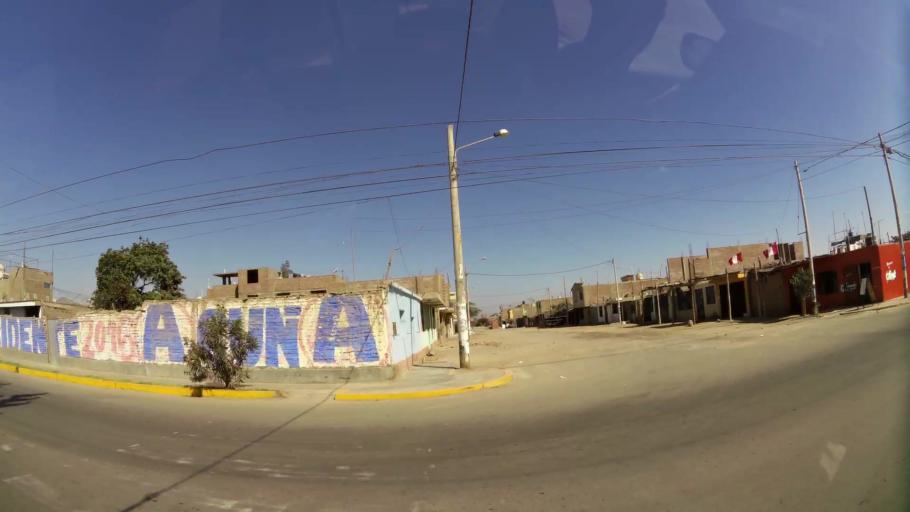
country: PE
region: Ica
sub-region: Provincia de Ica
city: La Tinguina
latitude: -14.0313
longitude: -75.7027
